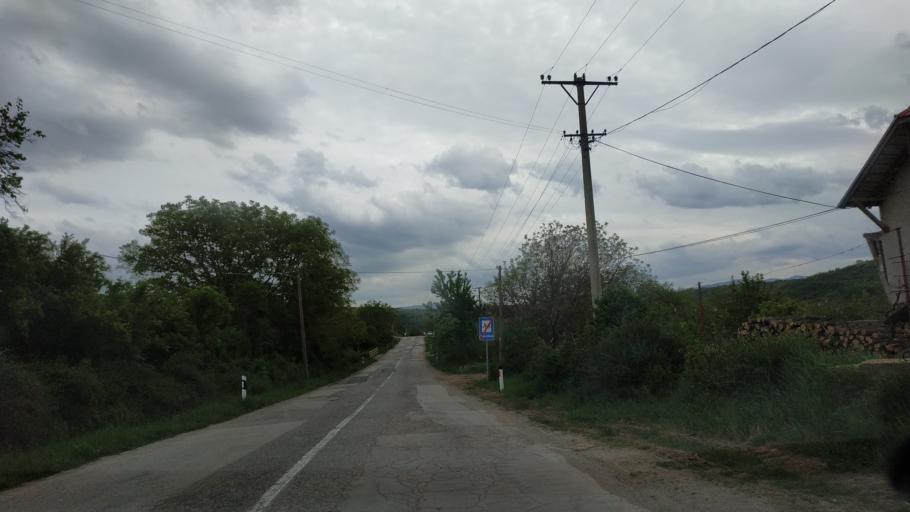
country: RS
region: Central Serbia
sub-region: Nisavski Okrug
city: Aleksinac
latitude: 43.6058
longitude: 21.6874
